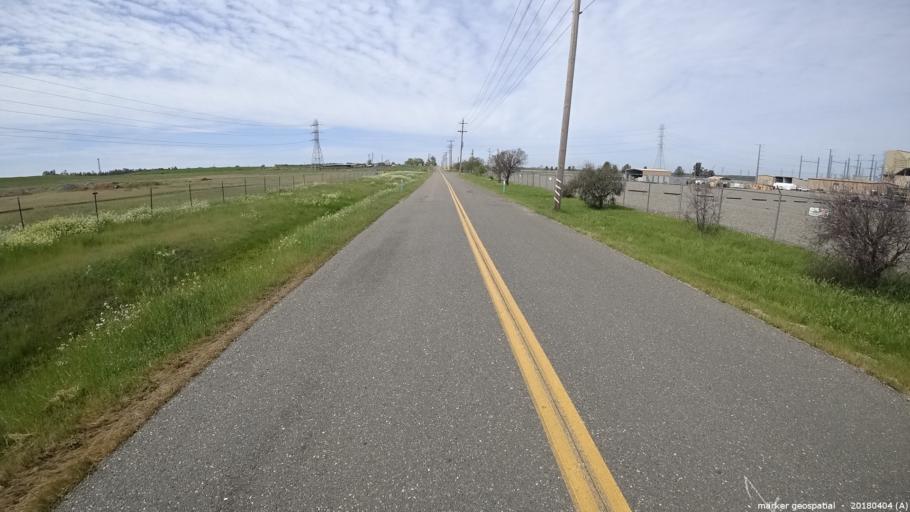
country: US
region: California
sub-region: Sacramento County
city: Clay
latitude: 38.3361
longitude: -121.1231
